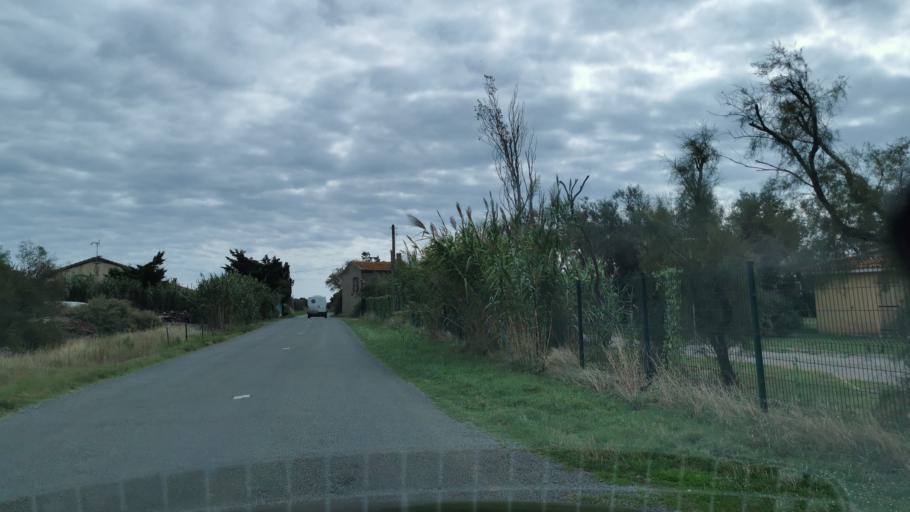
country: FR
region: Languedoc-Roussillon
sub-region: Departement de l'Herault
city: Vendres
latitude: 43.2234
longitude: 3.2149
